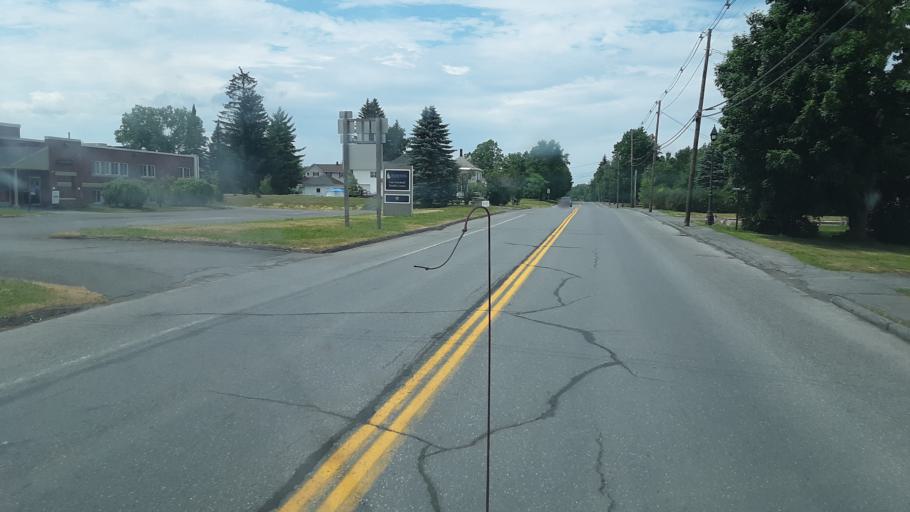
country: US
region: Maine
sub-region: Aroostook County
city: Fort Fairfield
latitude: 46.7732
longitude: -67.8366
